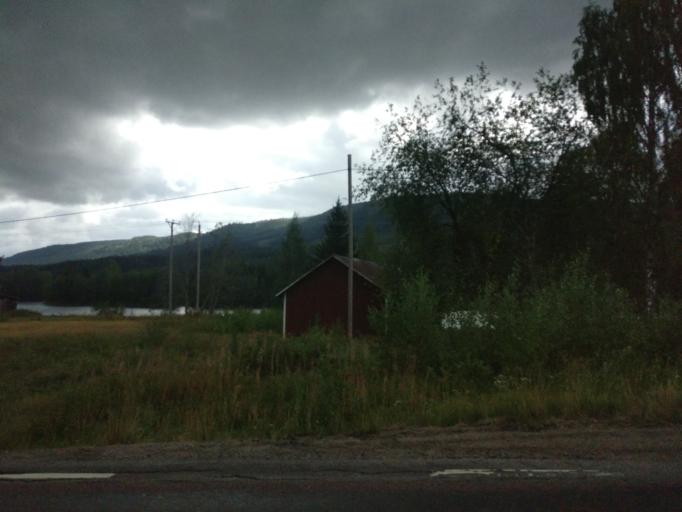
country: SE
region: Vaermland
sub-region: Torsby Kommun
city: Torsby
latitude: 60.7386
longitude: 12.8547
